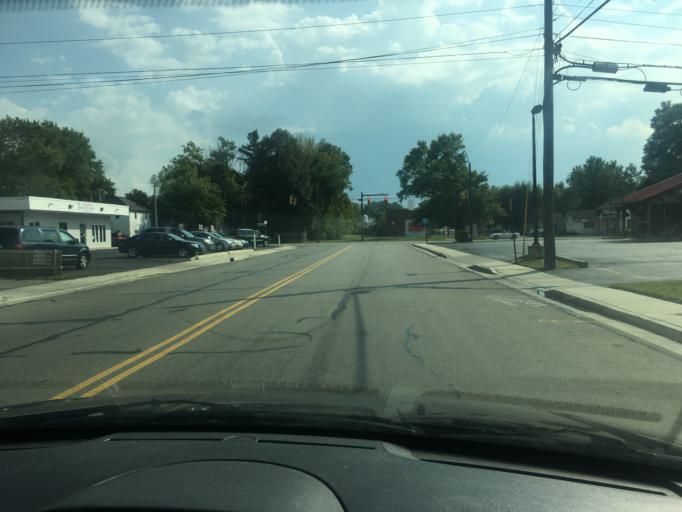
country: US
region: Ohio
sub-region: Champaign County
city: Urbana
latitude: 40.1096
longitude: -83.7651
